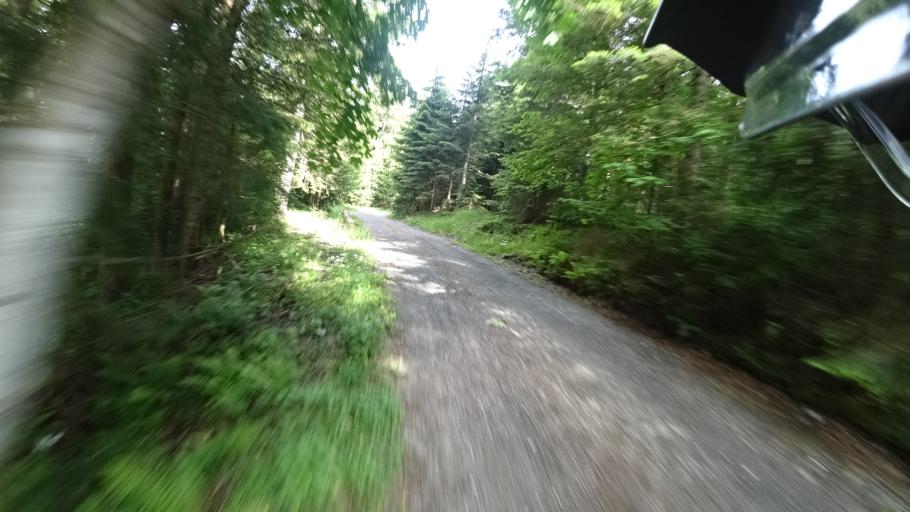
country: HR
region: Primorsko-Goranska
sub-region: Grad Delnice
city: Delnice
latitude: 45.2735
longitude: 14.8972
